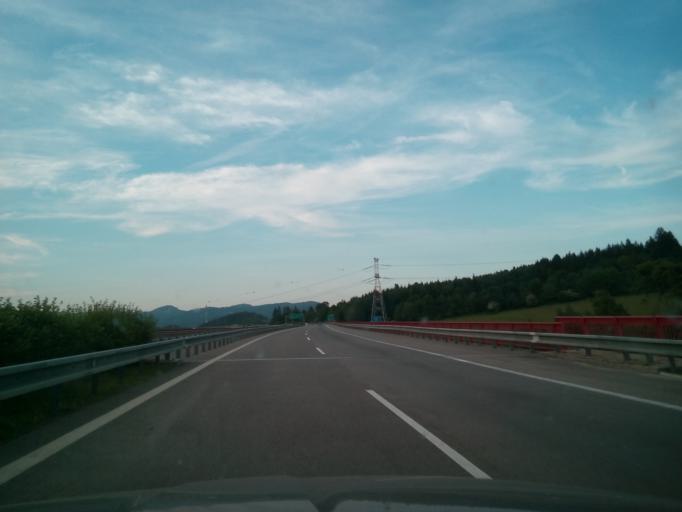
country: SK
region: Trenciansky
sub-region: Okres Povazska Bystrica
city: Povazska Bystrica
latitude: 49.0836
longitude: 18.4176
